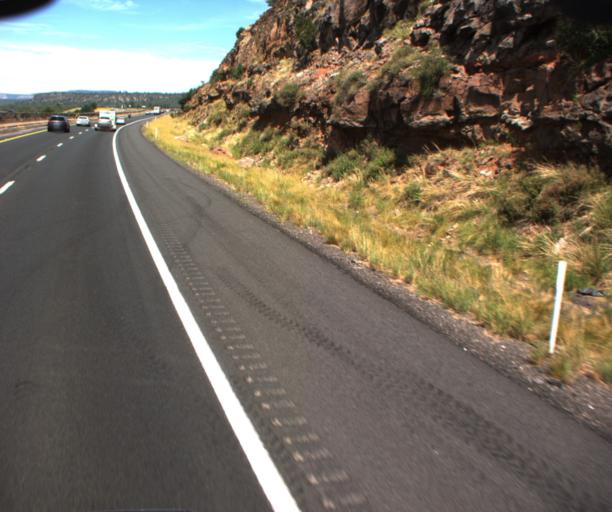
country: US
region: Arizona
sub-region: Yavapai County
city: Village of Oak Creek (Big Park)
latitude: 34.8096
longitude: -111.6048
